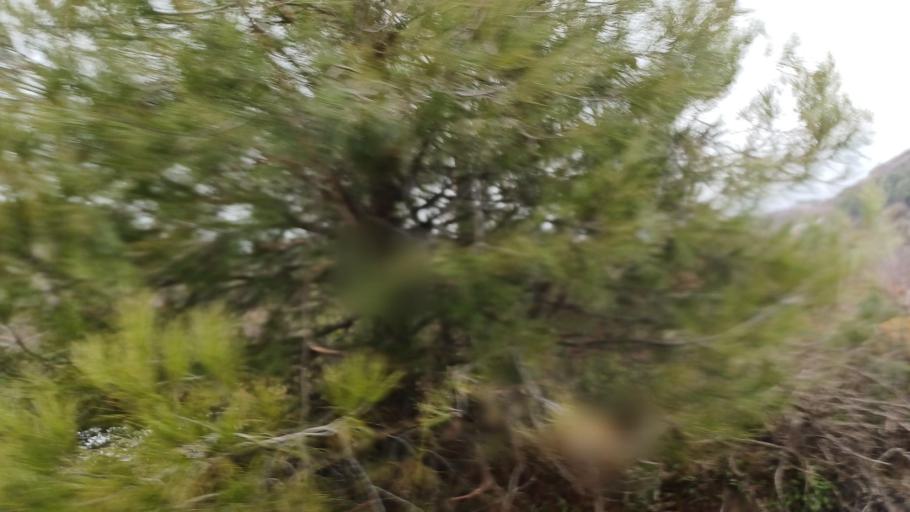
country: CY
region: Limassol
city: Kyperounta
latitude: 34.9269
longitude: 32.9704
